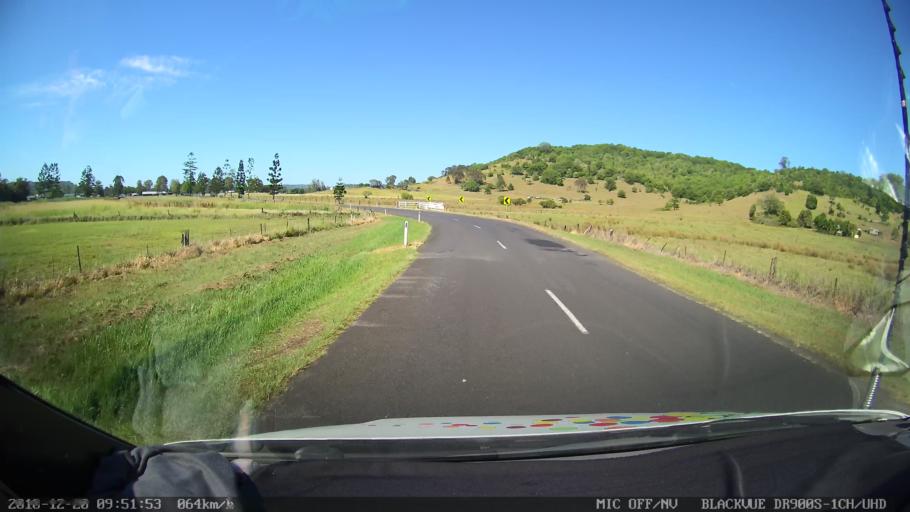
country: AU
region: New South Wales
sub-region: Lismore Municipality
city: Lismore
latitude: -28.7910
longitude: 153.2730
